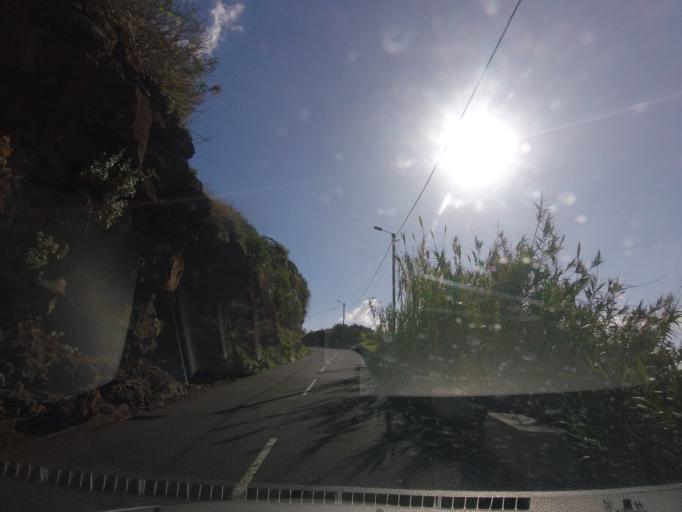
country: PT
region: Madeira
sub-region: Calheta
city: Estreito da Calheta
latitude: 32.7340
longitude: -17.1987
